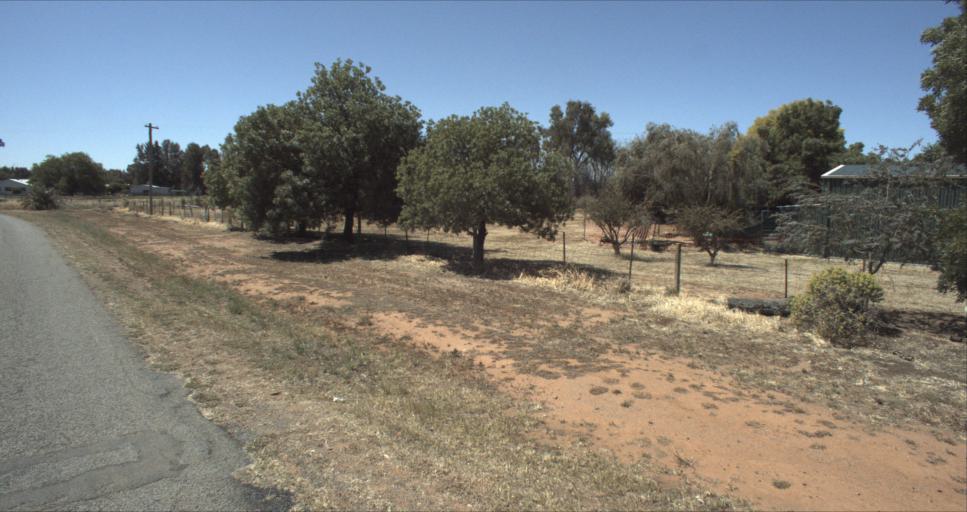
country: AU
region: New South Wales
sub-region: Leeton
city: Leeton
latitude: -34.5270
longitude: 146.3333
